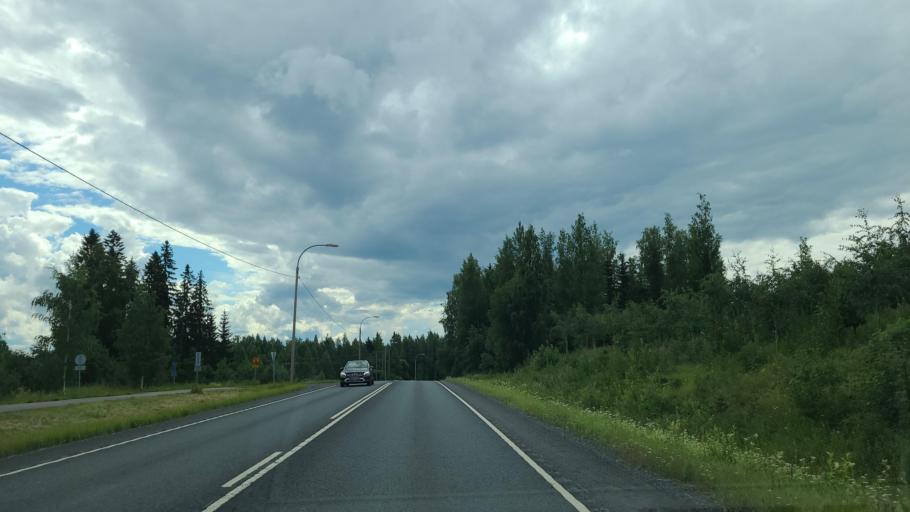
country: FI
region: Northern Savo
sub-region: Kuopio
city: Siilinjaervi
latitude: 63.1204
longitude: 27.7686
